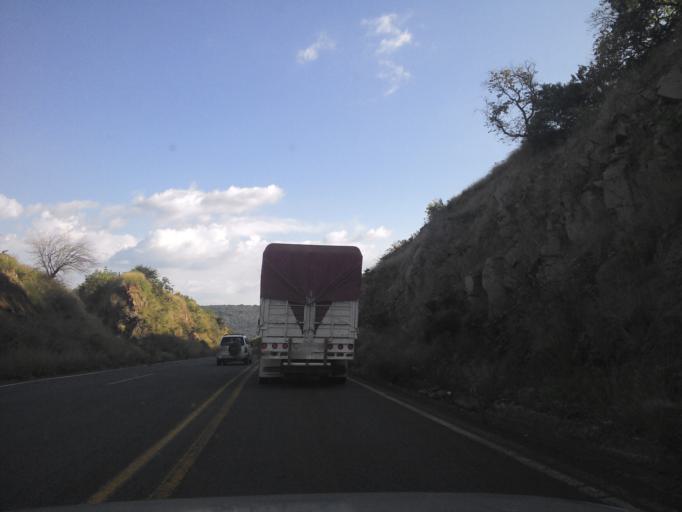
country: MX
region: Jalisco
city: Atotonilco el Alto
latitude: 20.5611
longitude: -102.5155
